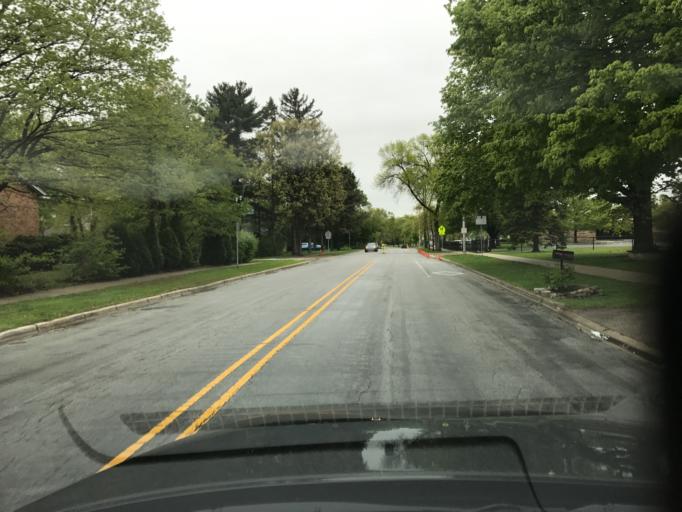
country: US
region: Illinois
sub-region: DuPage County
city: Naperville
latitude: 41.7655
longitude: -88.1285
